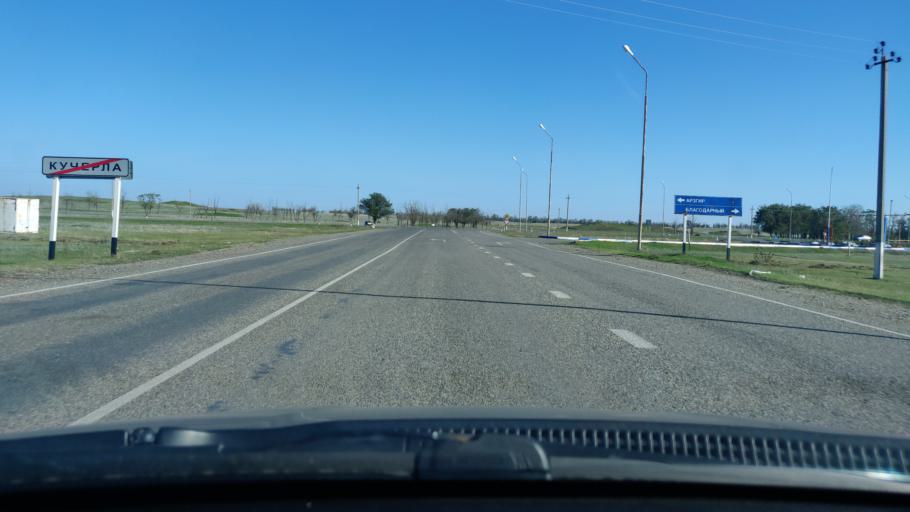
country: RU
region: Stavropol'skiy
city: Letnyaya Stavka
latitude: 45.3729
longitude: 43.6915
